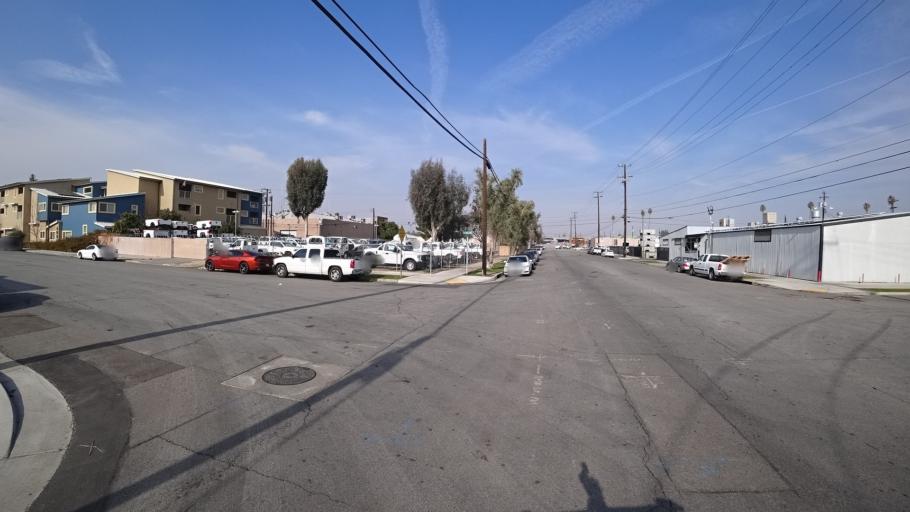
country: US
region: California
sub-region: Kern County
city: Bakersfield
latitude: 35.3770
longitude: -119.0049
